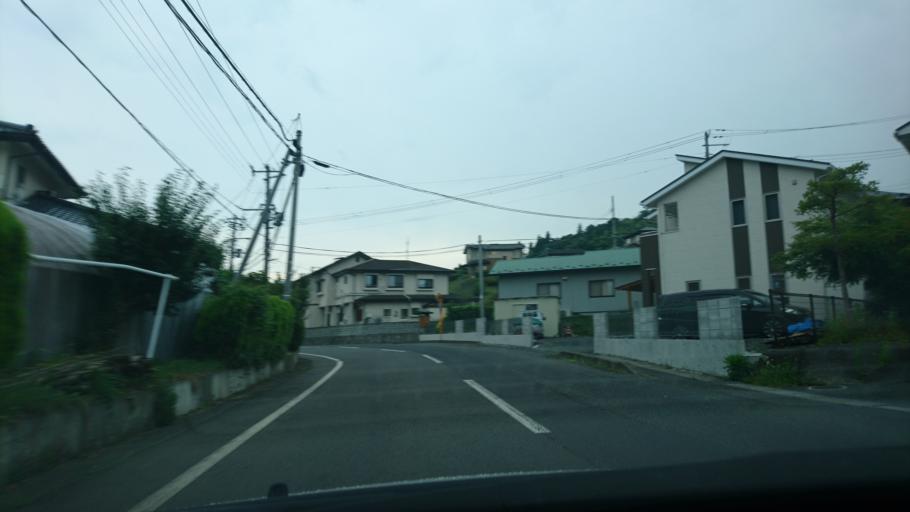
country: JP
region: Iwate
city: Ichinoseki
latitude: 38.9293
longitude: 141.1589
